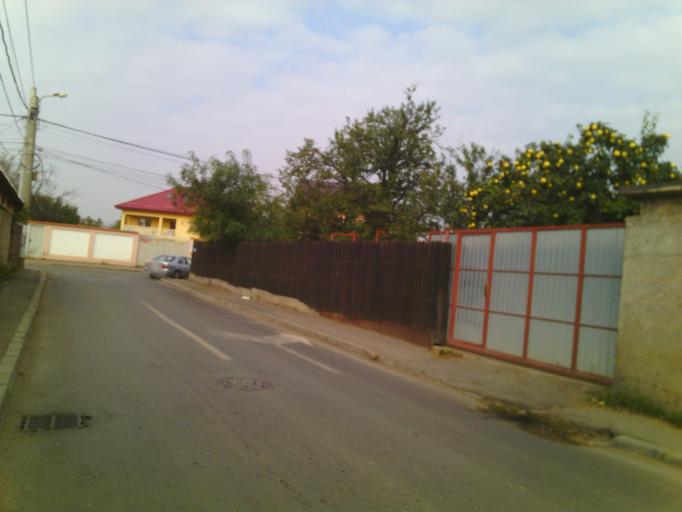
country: RO
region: Bucuresti
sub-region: Municipiul Bucuresti
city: Bucuresti
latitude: 44.3884
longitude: 26.0698
